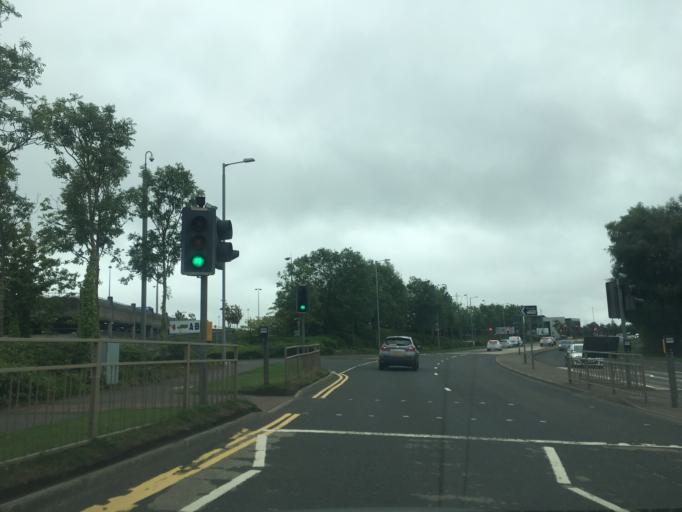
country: GB
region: Scotland
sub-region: Renfrewshire
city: Renfrew
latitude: 55.8758
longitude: -4.3686
